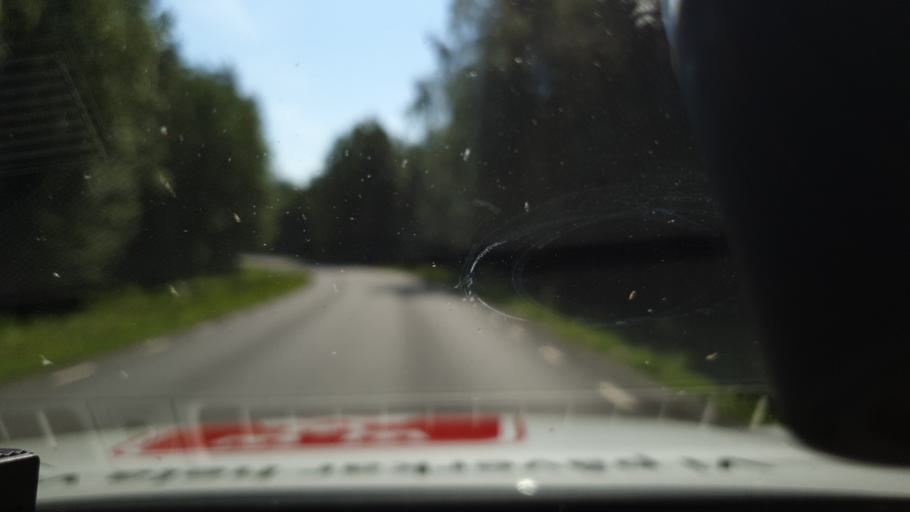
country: SE
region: Norrbotten
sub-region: Lulea Kommun
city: Gammelstad
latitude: 65.7884
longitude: 22.0871
